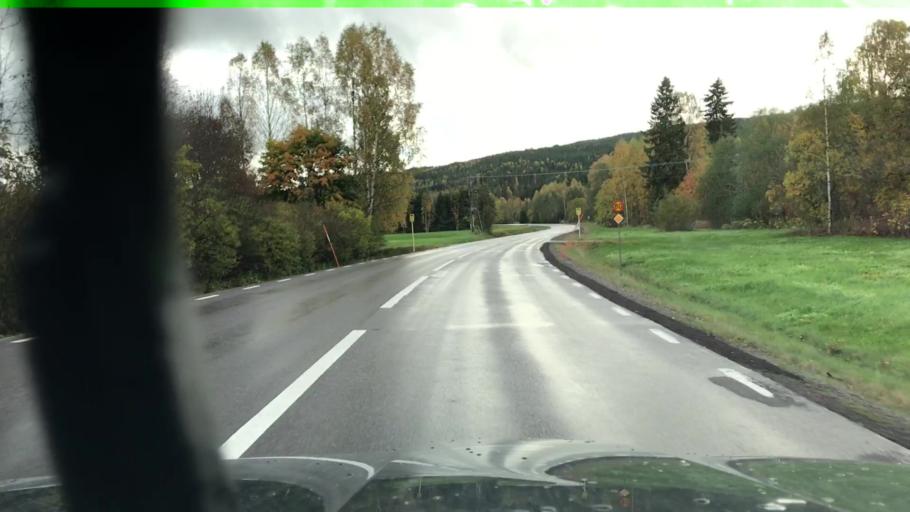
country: SE
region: Vaermland
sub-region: Hagfors Kommun
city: Ekshaerad
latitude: 60.4382
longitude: 13.2388
